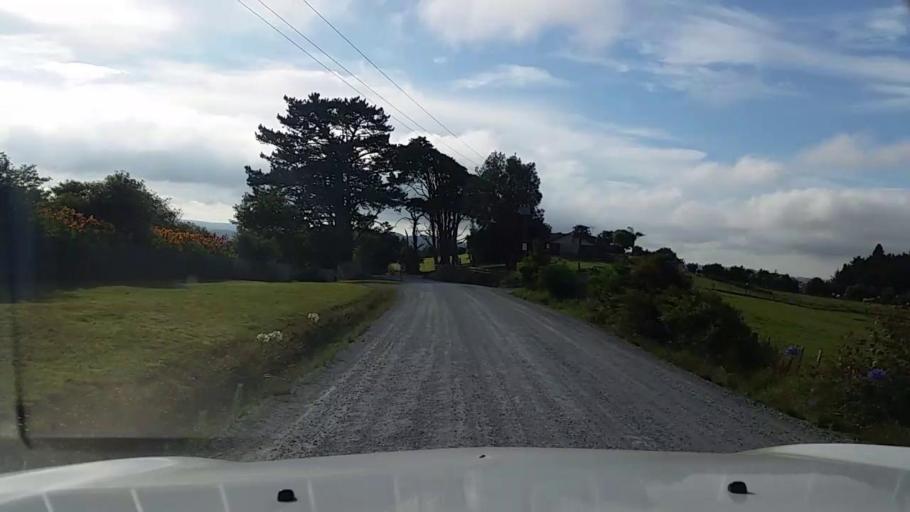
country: NZ
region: Northland
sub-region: Whangarei
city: Maungatapere
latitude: -35.6824
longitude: 174.1793
